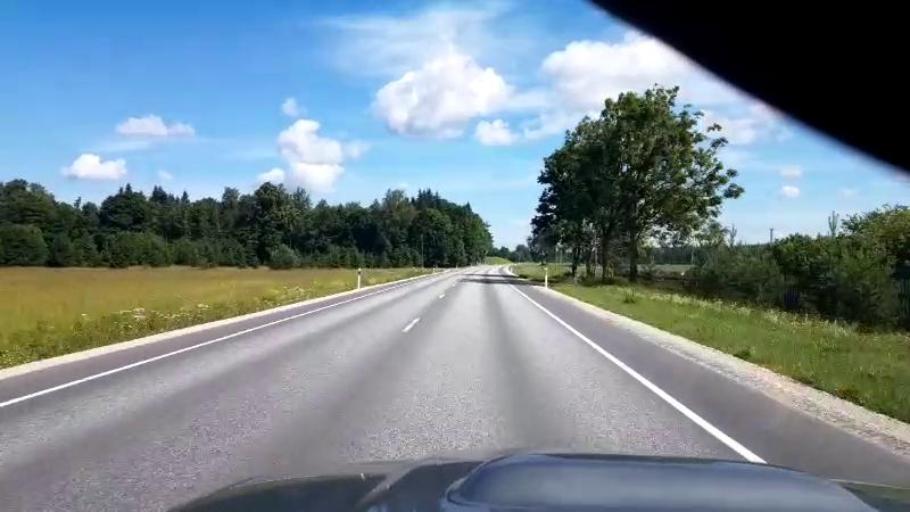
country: EE
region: Jaervamaa
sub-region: Paide linn
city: Paide
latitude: 58.9834
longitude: 25.6686
